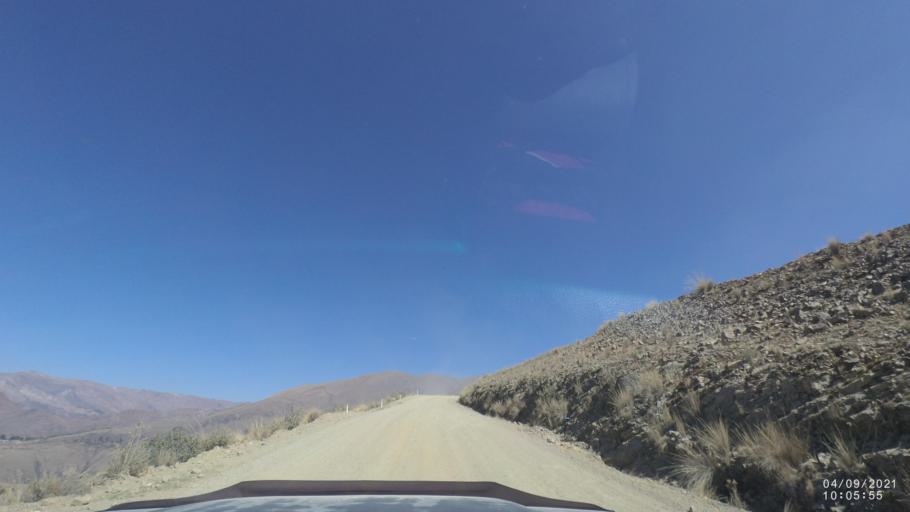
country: BO
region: Cochabamba
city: Sipe Sipe
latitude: -17.3527
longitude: -66.3899
